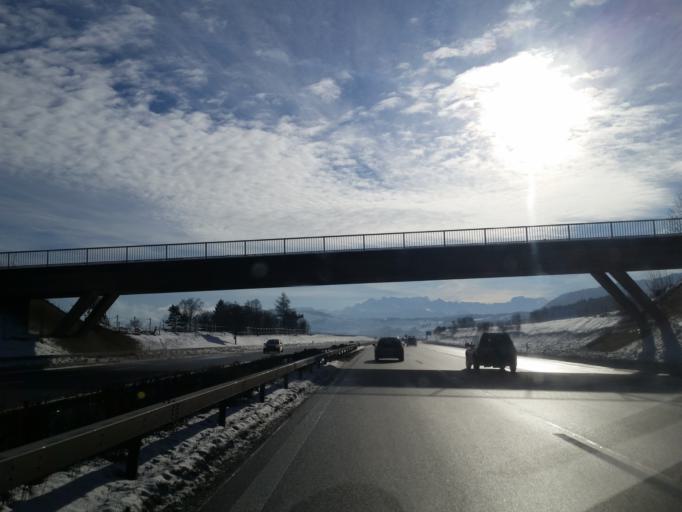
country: CH
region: Zurich
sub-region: Bezirk Horgen
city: Waedenswil / Untermosen-Fuhr
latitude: 47.2193
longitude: 8.6631
